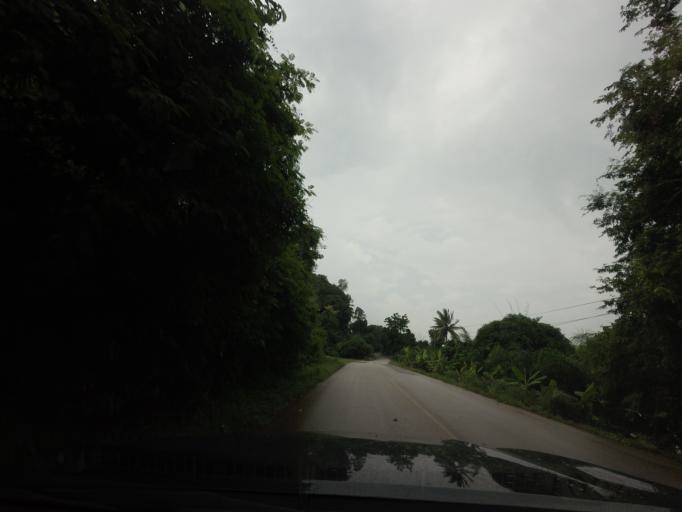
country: TH
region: Loei
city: Pak Chom
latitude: 18.1148
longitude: 101.9895
